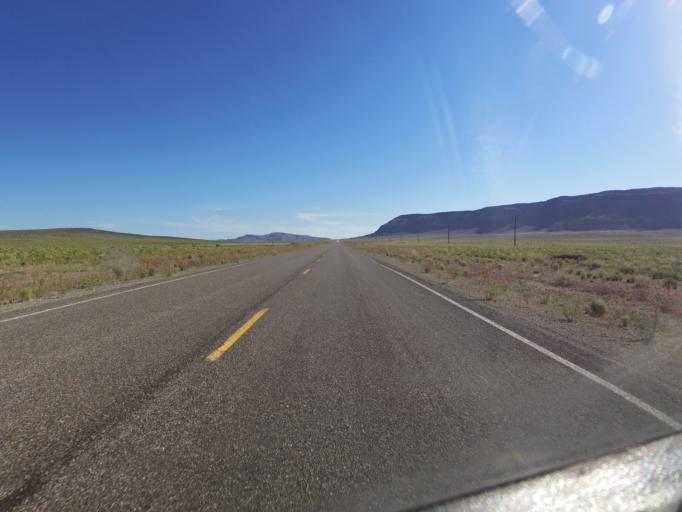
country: US
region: Nevada
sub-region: Nye County
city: Tonopah
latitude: 38.3788
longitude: -116.2213
